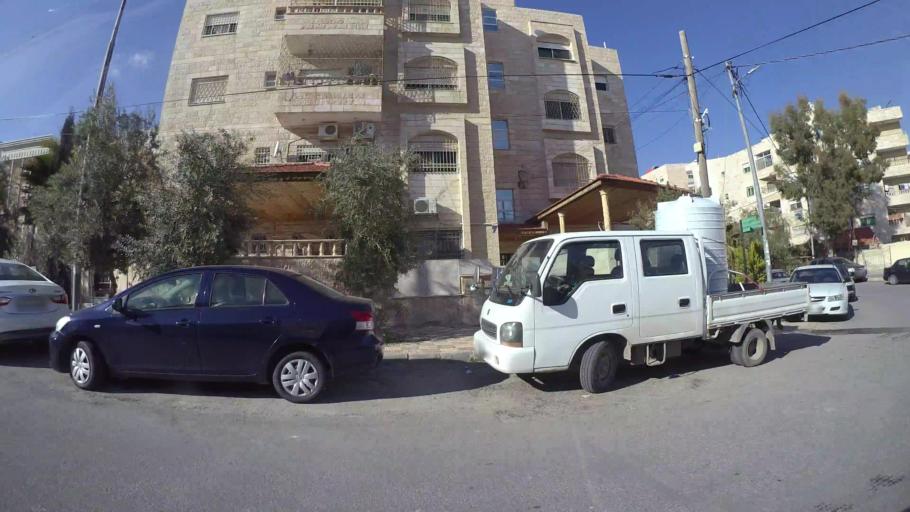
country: JO
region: Amman
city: Amman
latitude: 31.9789
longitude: 35.9340
